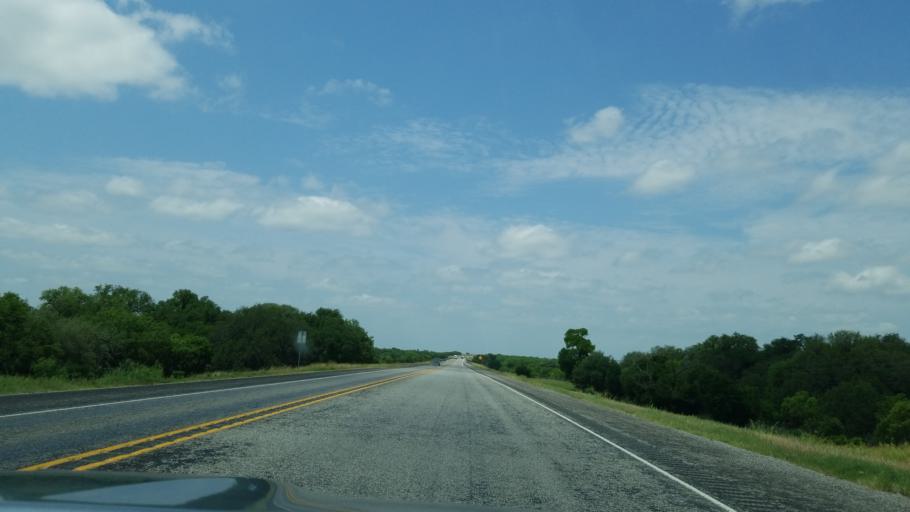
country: US
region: Texas
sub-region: Zavala County
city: La Pryor
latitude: 28.9352
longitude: -99.7891
